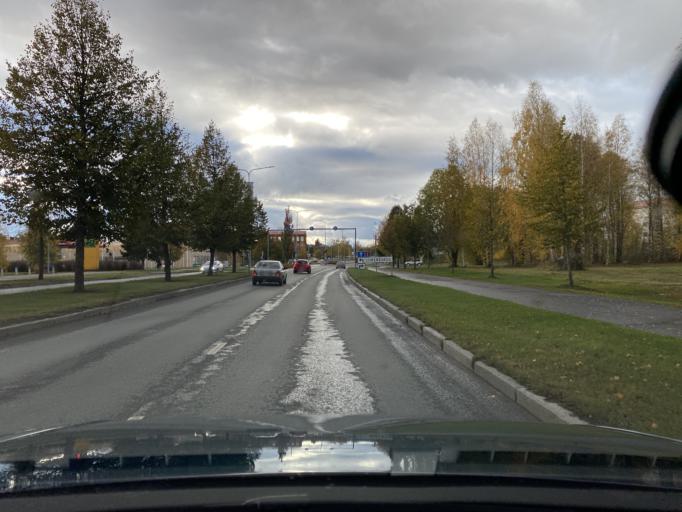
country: FI
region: Haeme
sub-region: Forssa
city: Forssa
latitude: 60.8128
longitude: 23.6329
